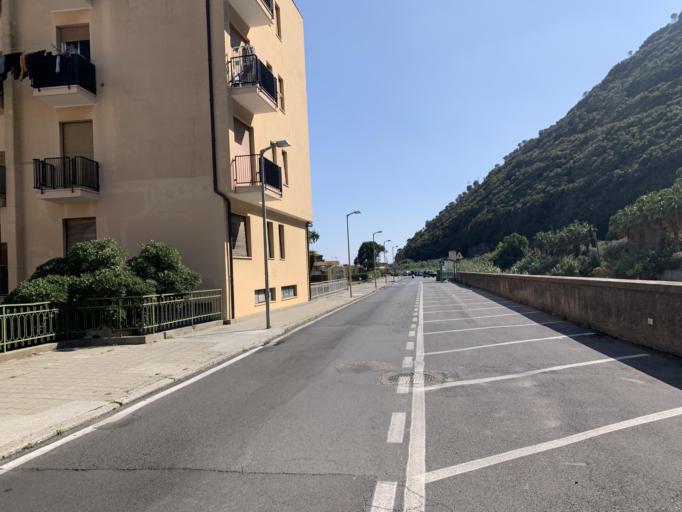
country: IT
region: Liguria
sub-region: Provincia di Savona
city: Finale Ligure
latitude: 44.1730
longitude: 8.3314
